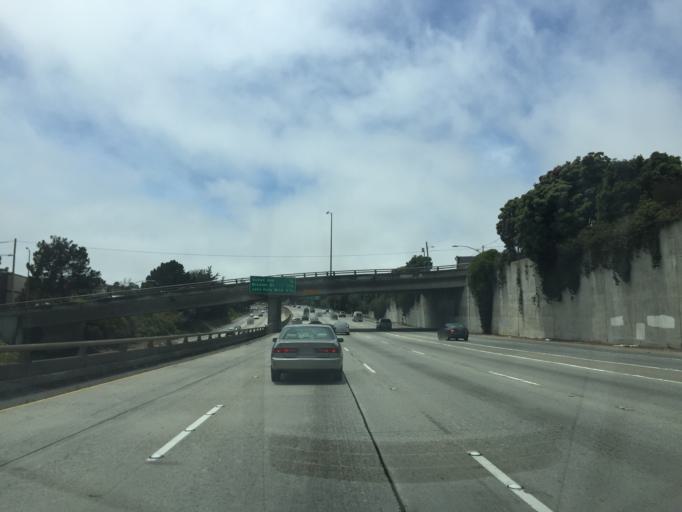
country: US
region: California
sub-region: San Mateo County
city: Daly City
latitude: 37.7305
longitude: -122.4384
